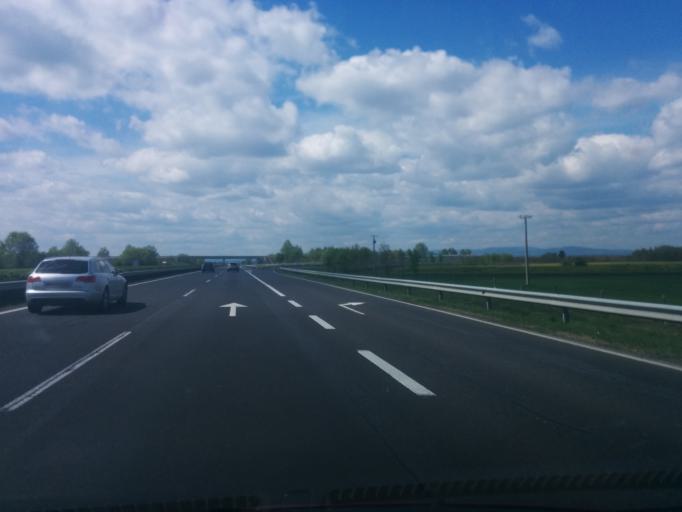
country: HU
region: Borsod-Abauj-Zemplen
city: Hejobaba
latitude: 47.8792
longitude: 20.9050
